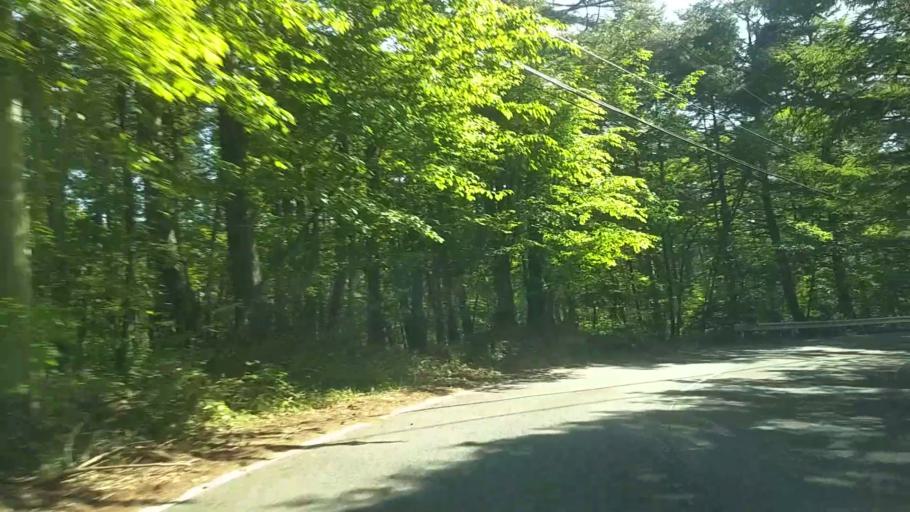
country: JP
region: Yamanashi
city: Nirasaki
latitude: 35.8818
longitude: 138.3739
